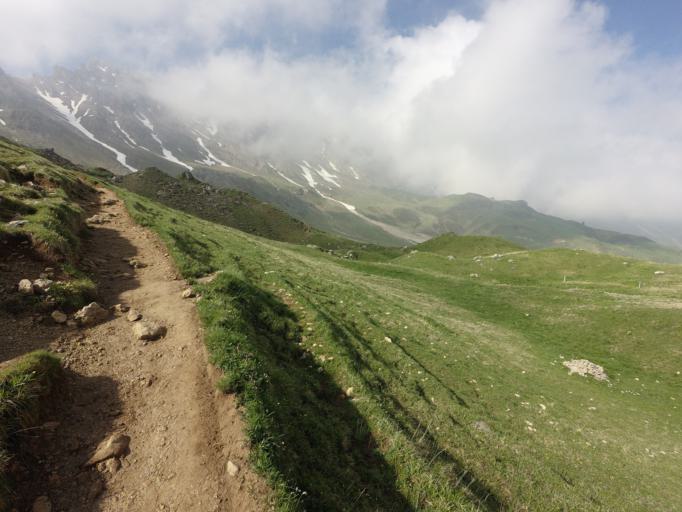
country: IT
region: Trentino-Alto Adige
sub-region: Bolzano
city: Ortisei
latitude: 46.5109
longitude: 11.6348
